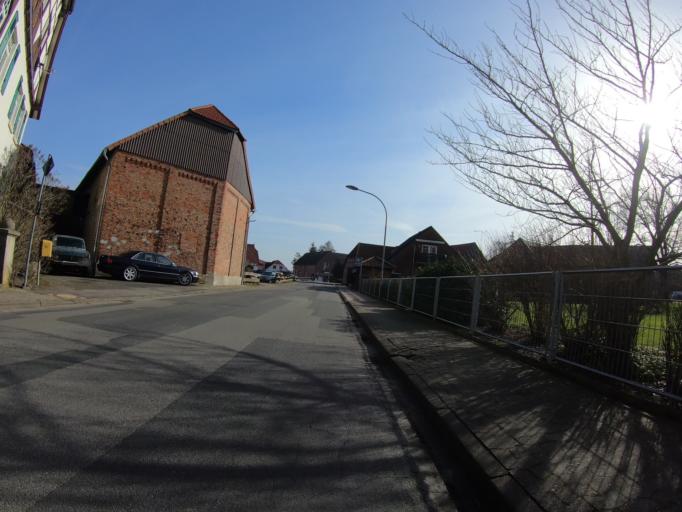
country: DE
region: Lower Saxony
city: Wasbuttel
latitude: 52.4088
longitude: 10.5636
